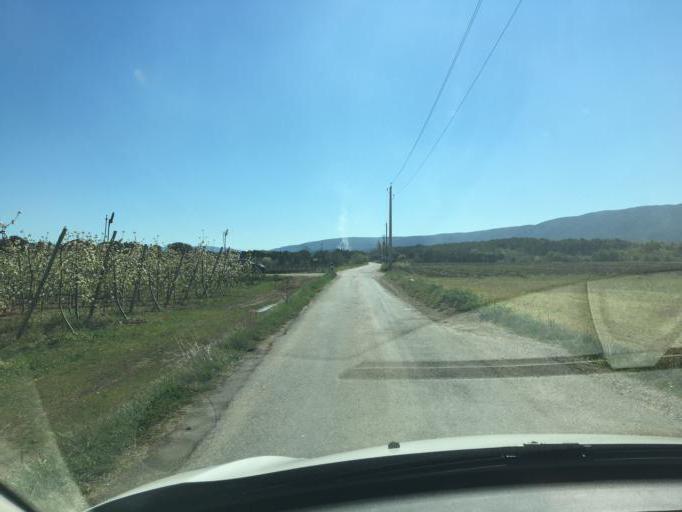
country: FR
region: Provence-Alpes-Cote d'Azur
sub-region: Departement du Vaucluse
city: Maubec
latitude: 43.8632
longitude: 5.1270
